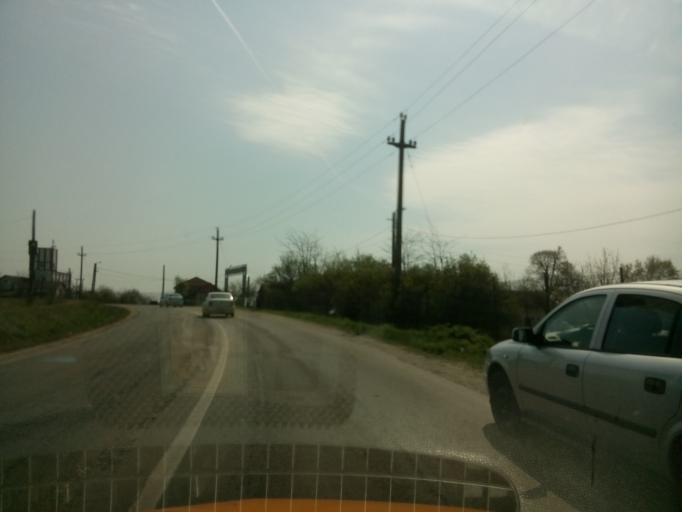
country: RO
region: Calarasi
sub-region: Comuna Soldanu
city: Negoesti
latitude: 44.2313
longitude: 26.4894
